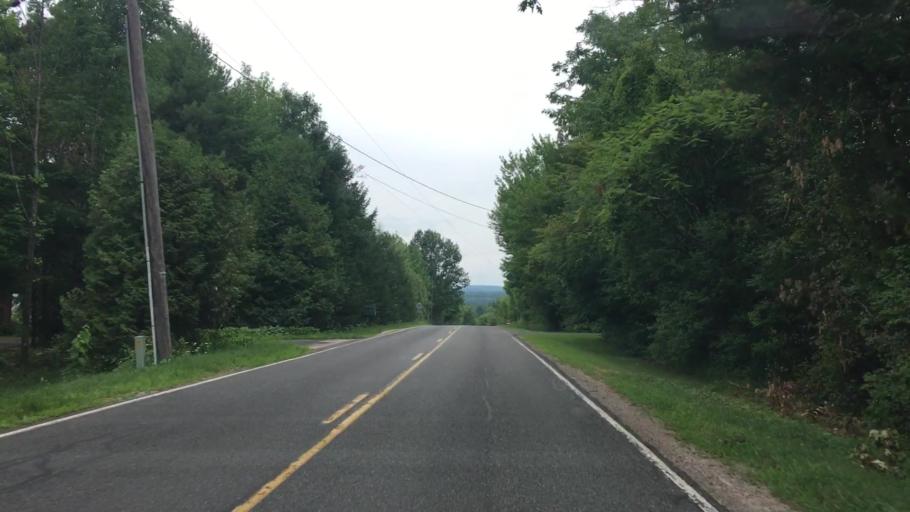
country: US
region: New York
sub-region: Clinton County
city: Peru
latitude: 44.5424
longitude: -73.5673
